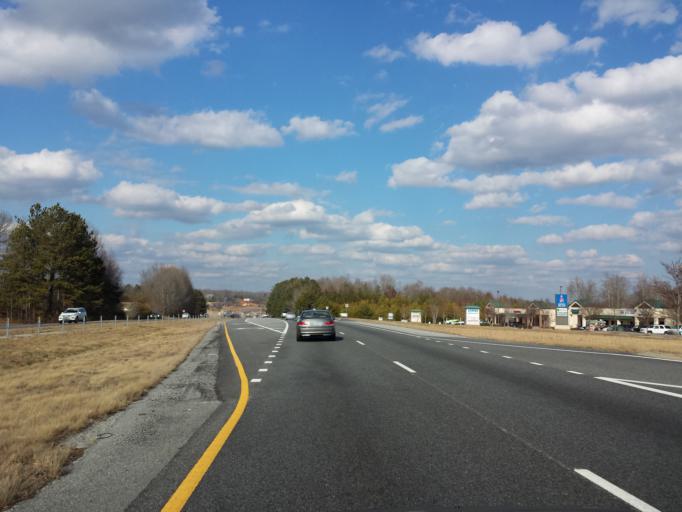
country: US
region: Georgia
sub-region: Dawson County
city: Dawsonville
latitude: 34.3475
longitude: -84.0493
